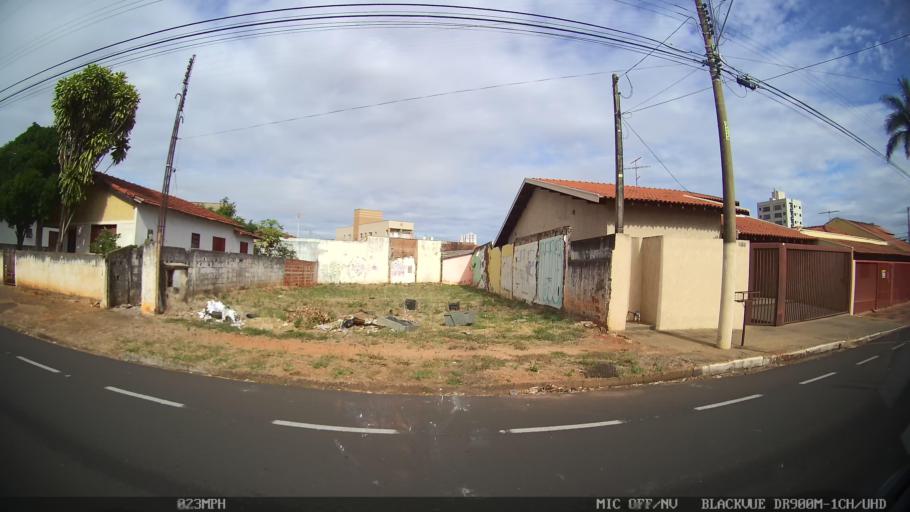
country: BR
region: Sao Paulo
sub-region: Sao Jose Do Rio Preto
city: Sao Jose do Rio Preto
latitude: -20.8349
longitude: -49.3800
